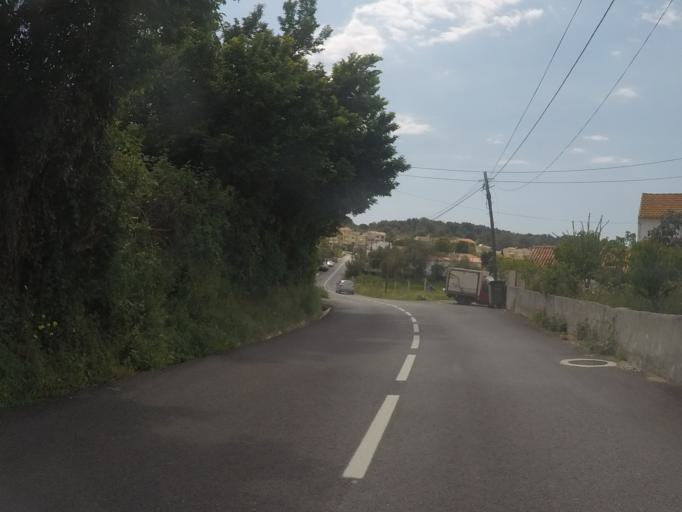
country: PT
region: Setubal
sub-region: Sesimbra
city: Sesimbra
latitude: 38.4613
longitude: -9.0710
